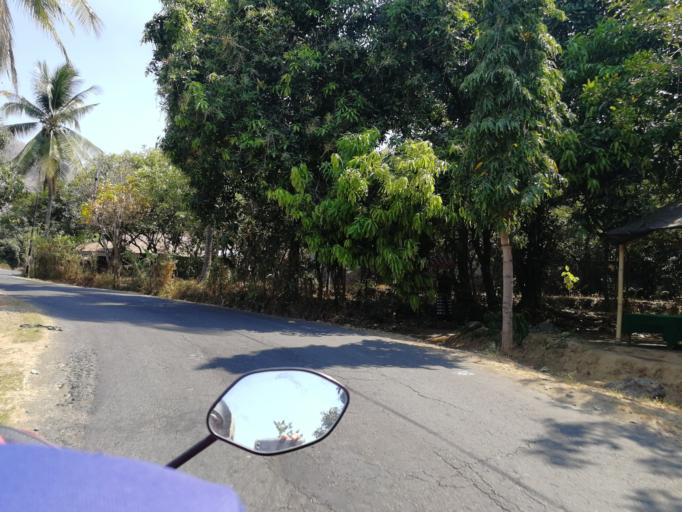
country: ID
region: Bali
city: Banjar Trunyan
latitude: -8.1256
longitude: 115.3290
